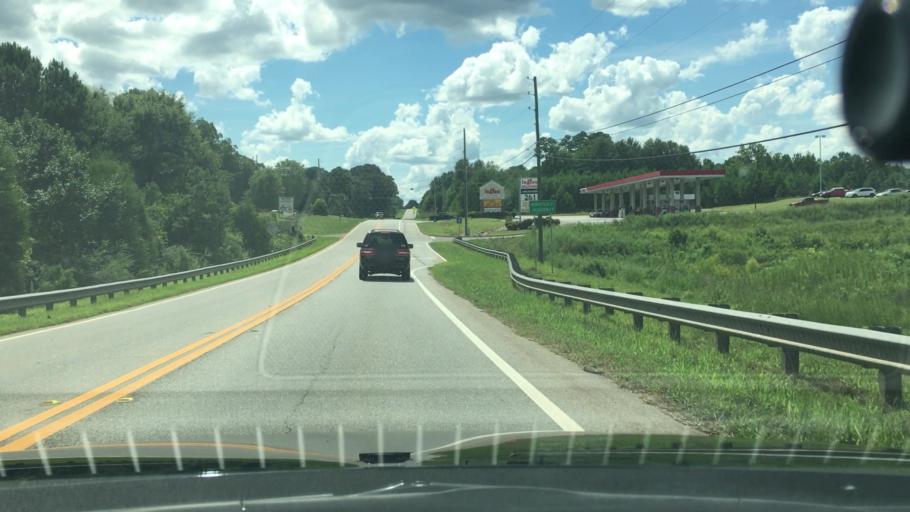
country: US
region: Georgia
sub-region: Putnam County
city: Eatonton
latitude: 33.3195
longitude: -83.4097
